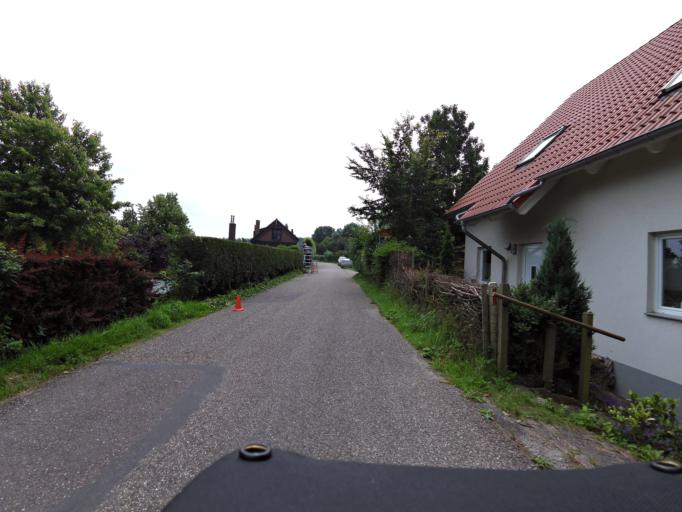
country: NL
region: South Holland
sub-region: Gemeente Hellevoetsluis
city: Nieuw-Helvoet
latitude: 51.8375
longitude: 4.0965
